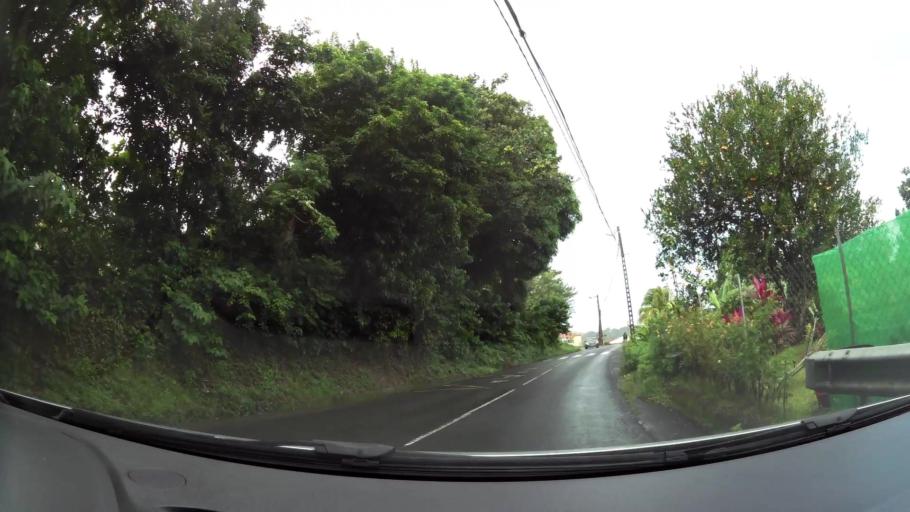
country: MQ
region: Martinique
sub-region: Martinique
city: Saint-Joseph
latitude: 14.6532
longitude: -61.0369
